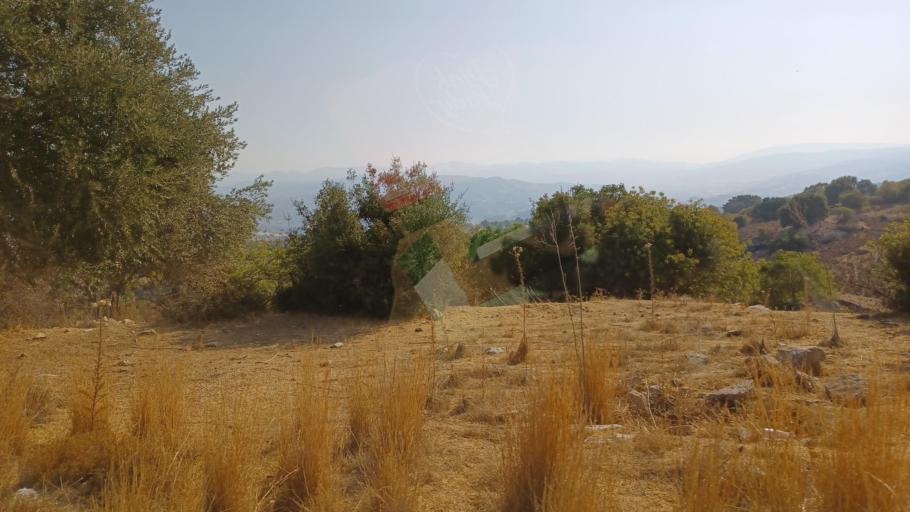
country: CY
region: Pafos
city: Polis
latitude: 34.9718
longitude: 32.4191
